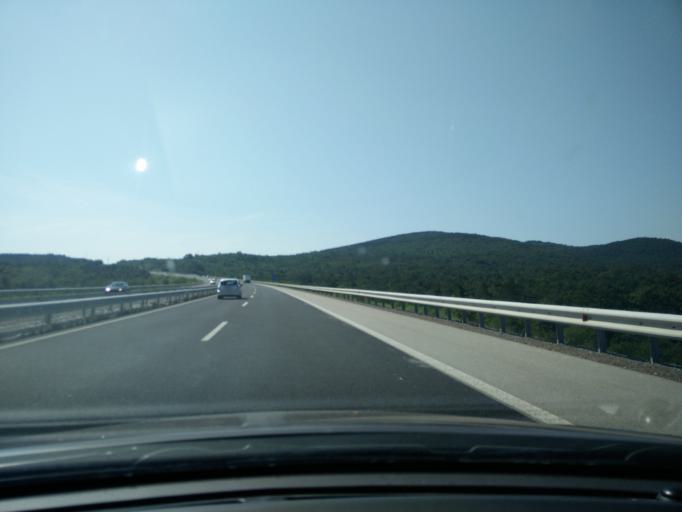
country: SI
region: Divaca
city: Divaca
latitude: 45.6526
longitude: 13.9608
